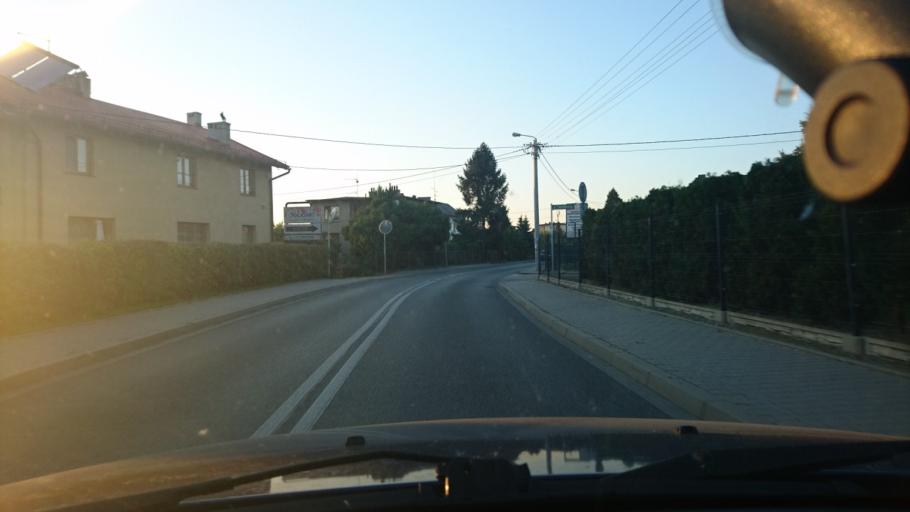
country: PL
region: Silesian Voivodeship
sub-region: Bielsko-Biala
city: Bielsko-Biala
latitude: 49.8515
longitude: 19.0503
